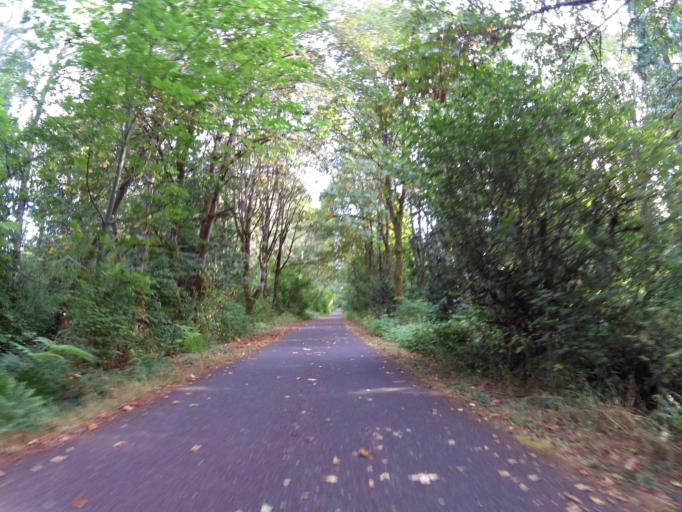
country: US
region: Washington
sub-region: Thurston County
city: Lacey
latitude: 46.9766
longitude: -122.8128
